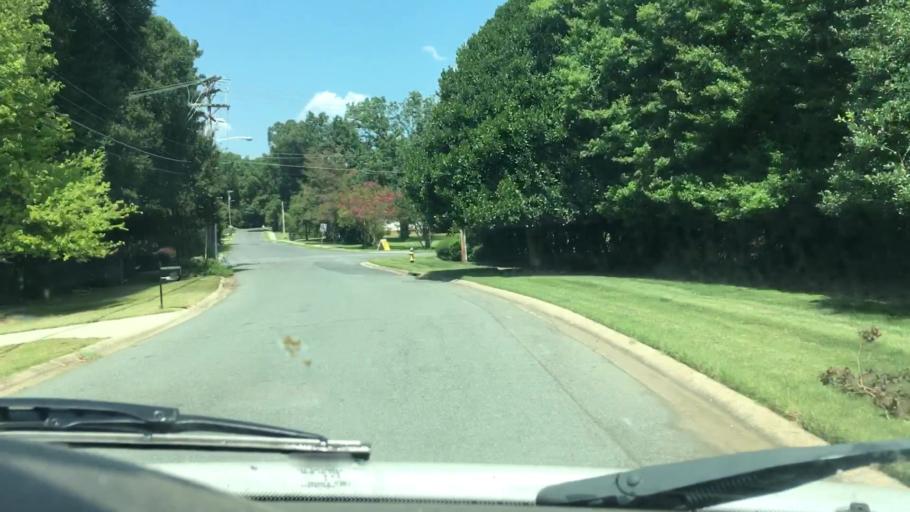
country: US
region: North Carolina
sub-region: Mecklenburg County
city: Cornelius
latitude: 35.4780
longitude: -80.8675
